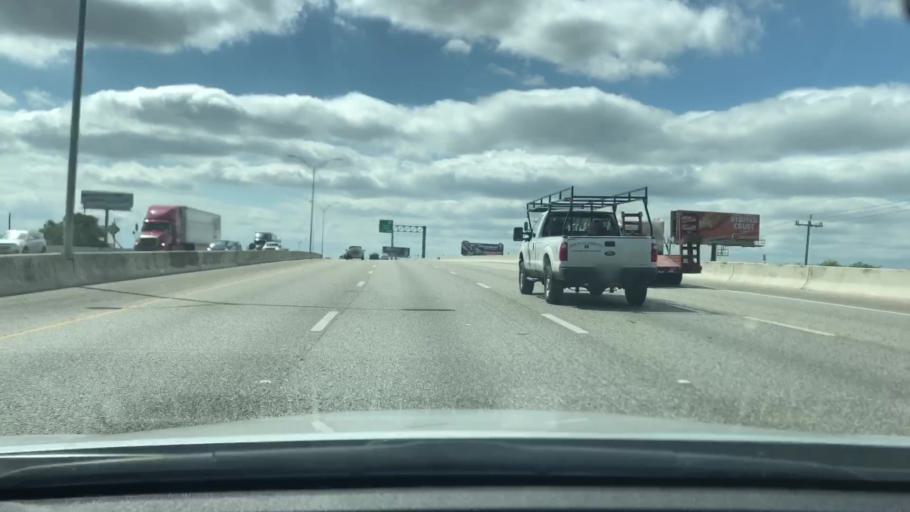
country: US
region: Texas
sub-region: Bexar County
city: Windcrest
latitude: 29.5349
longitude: -98.3889
